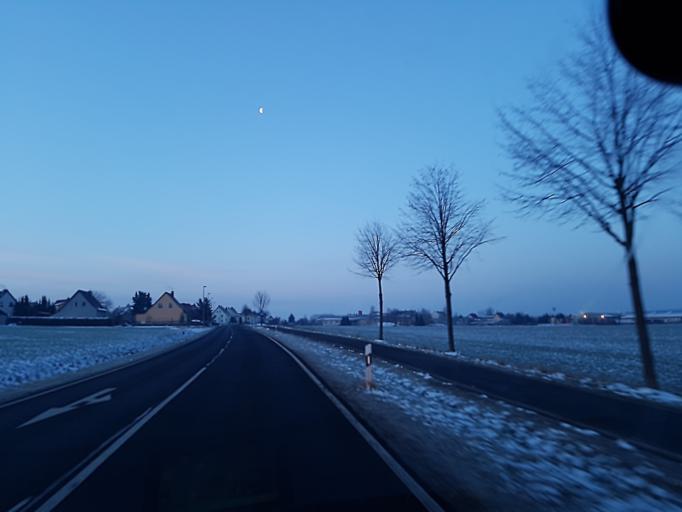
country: DE
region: Saxony
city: Oschatz
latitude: 51.3205
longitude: 13.1115
